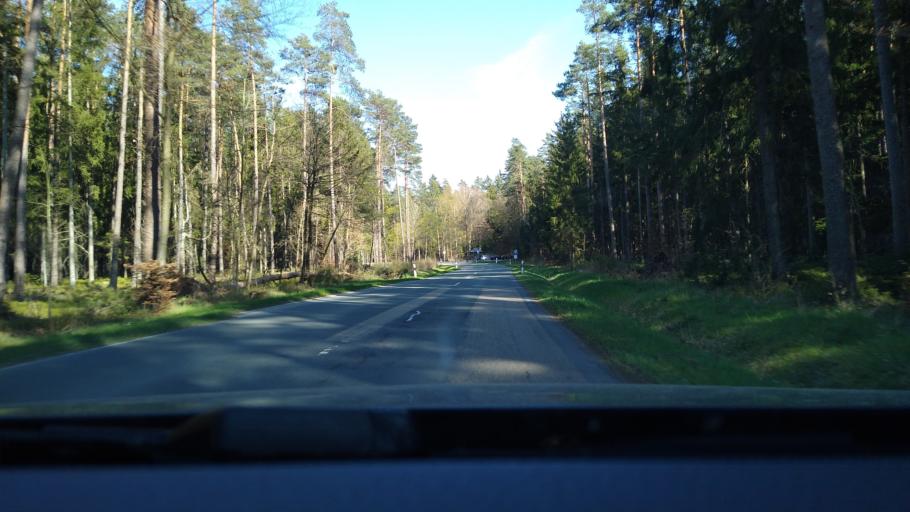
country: DE
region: Bavaria
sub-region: Regierungsbezirk Mittelfranken
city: Wolframs-Eschenbach
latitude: 49.1982
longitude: 10.7453
